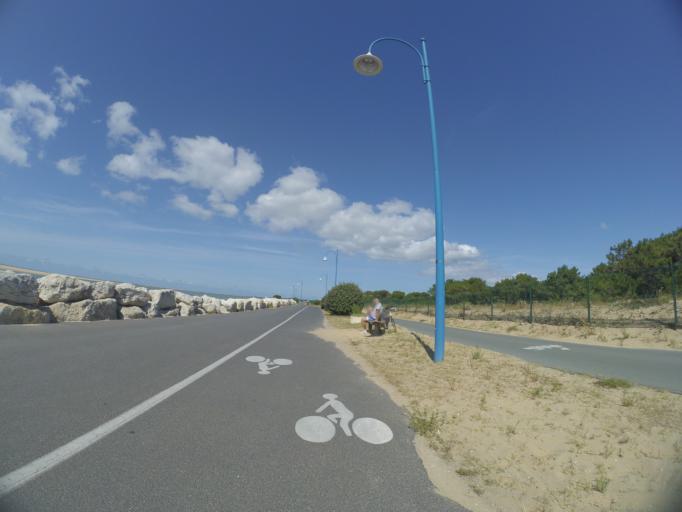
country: FR
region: Poitou-Charentes
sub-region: Departement de la Charente-Maritime
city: Les Mathes
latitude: 45.6775
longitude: -1.1705
